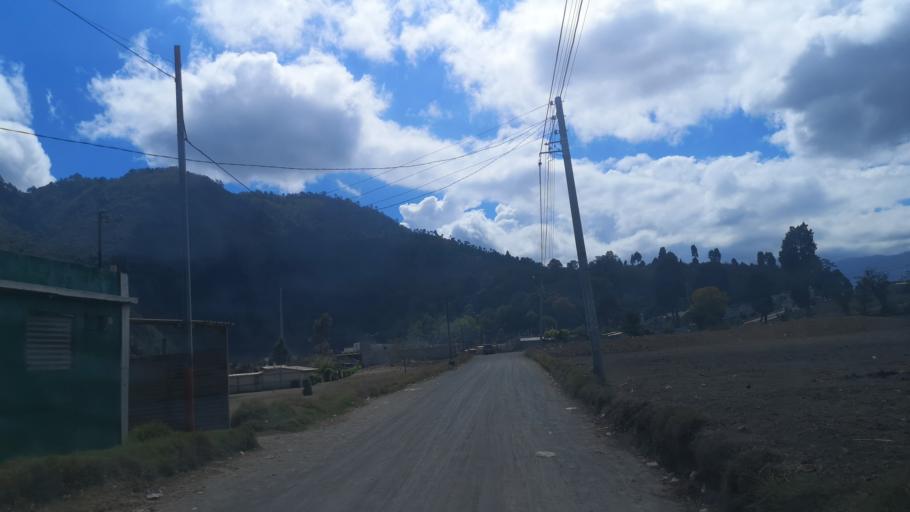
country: GT
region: Quetzaltenango
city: Almolonga
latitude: 14.7845
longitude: -91.5379
